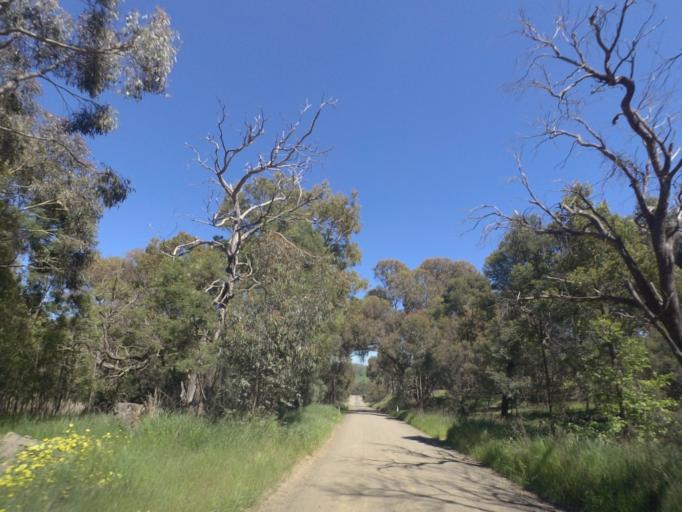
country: AU
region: Victoria
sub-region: Whittlesea
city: Whittlesea
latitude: -37.2835
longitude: 145.0047
